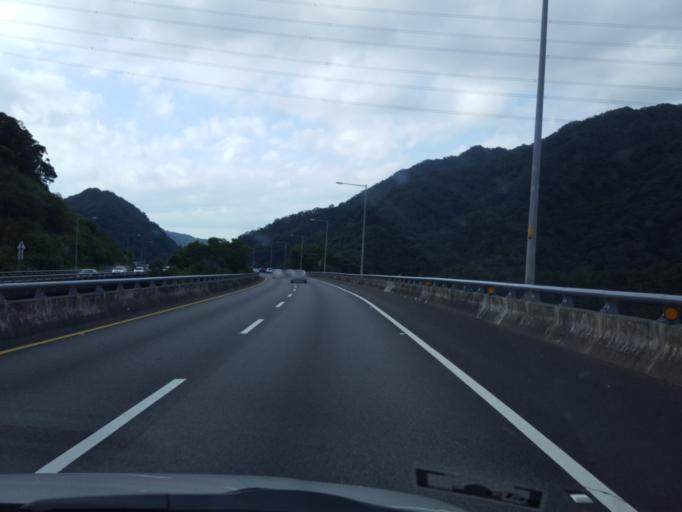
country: TW
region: Taipei
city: Taipei
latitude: 24.9787
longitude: 121.6760
